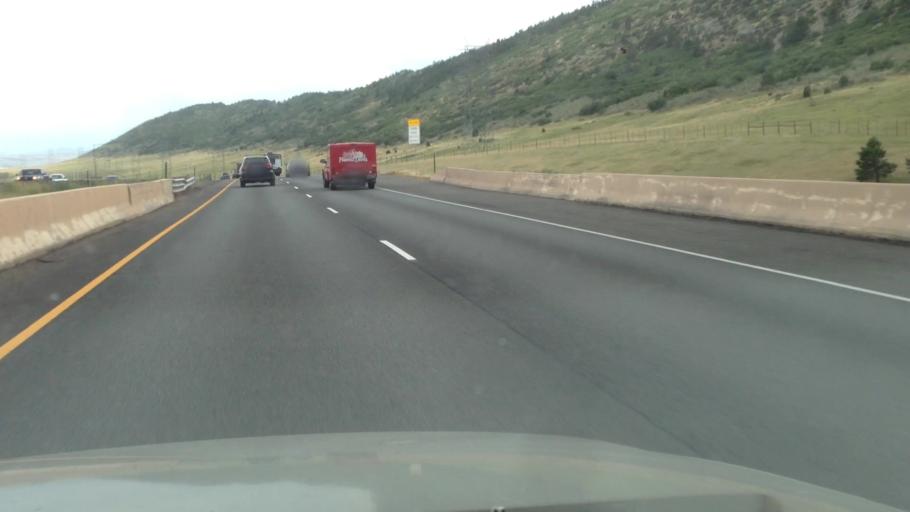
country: US
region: Colorado
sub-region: Jefferson County
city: Ken Caryl
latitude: 39.5783
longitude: -105.1419
